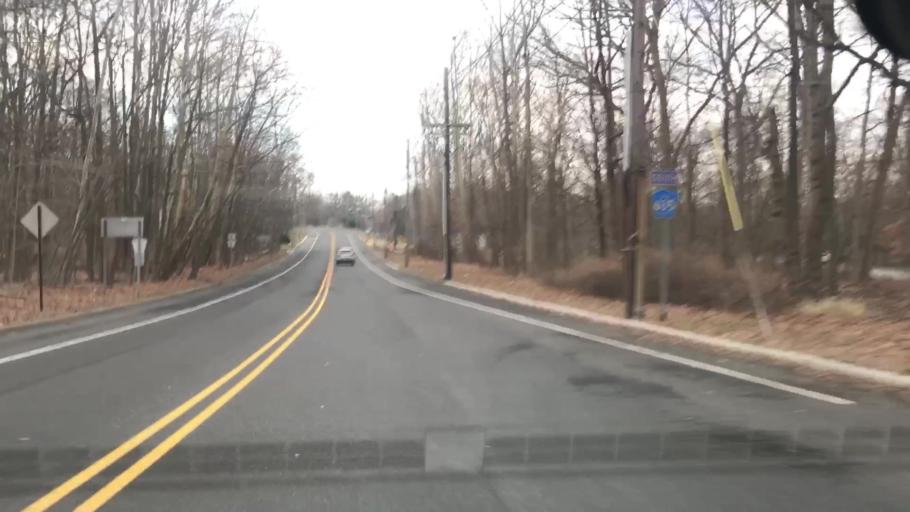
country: US
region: New Jersey
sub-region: Essex County
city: Roseland
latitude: 40.8029
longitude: -74.2944
